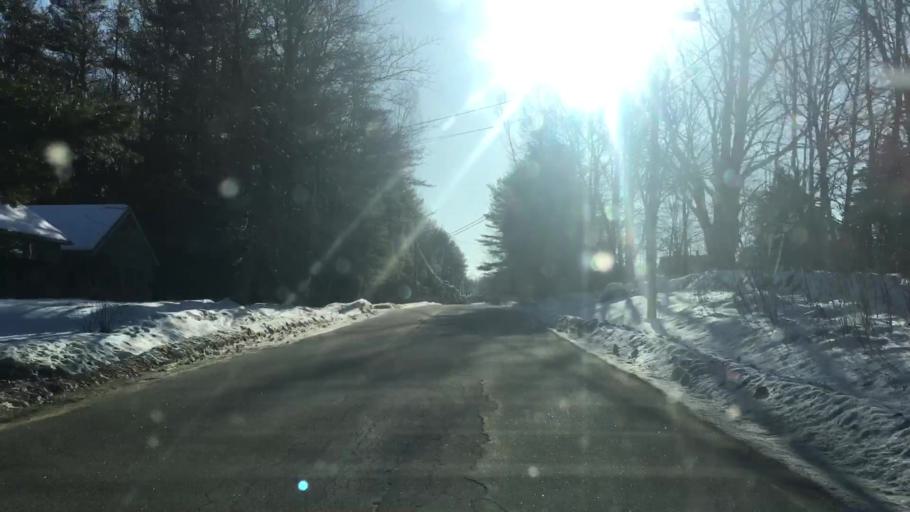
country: US
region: Maine
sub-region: Oxford County
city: Paris
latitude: 44.2739
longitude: -70.5061
